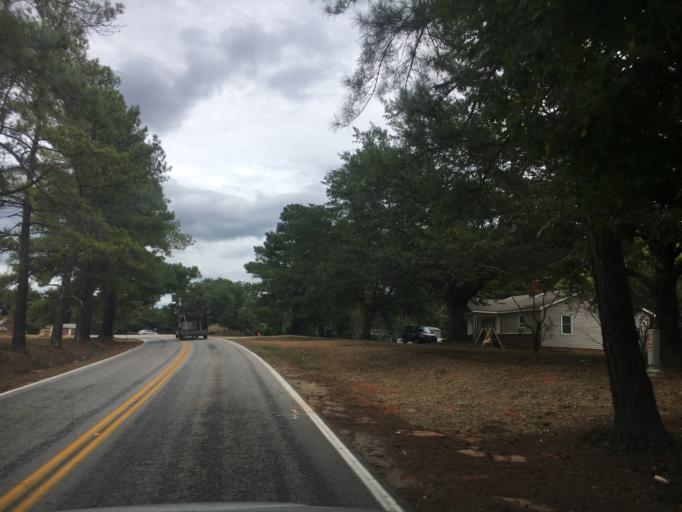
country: US
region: South Carolina
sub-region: Laurens County
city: Watts Mills
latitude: 34.5051
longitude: -81.9718
